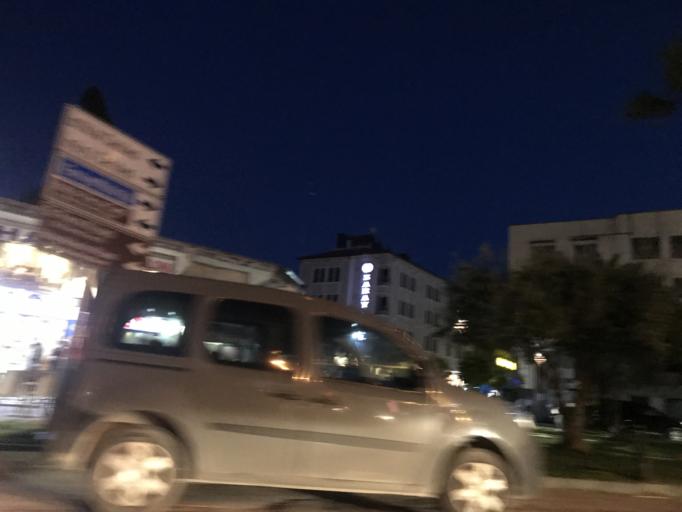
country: TR
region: Hatay
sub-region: Antakya Ilcesi
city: Antakya
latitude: 36.2022
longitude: 36.1613
